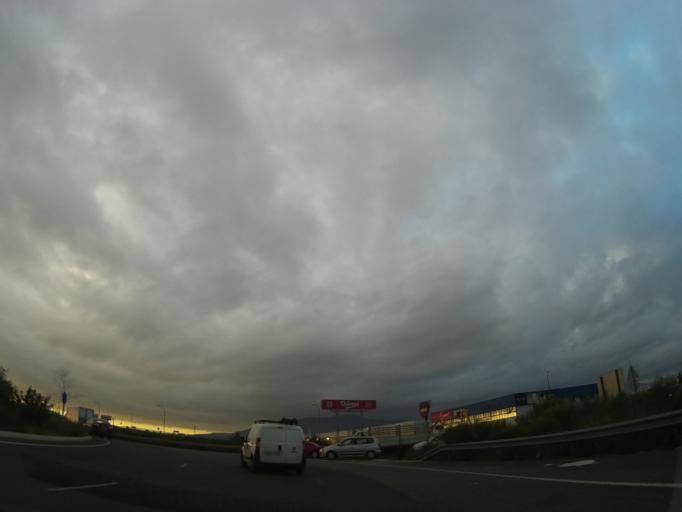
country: ES
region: Andalusia
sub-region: Provincia de Malaga
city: Alhaurin de la Torre
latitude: 36.7100
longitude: -4.5144
